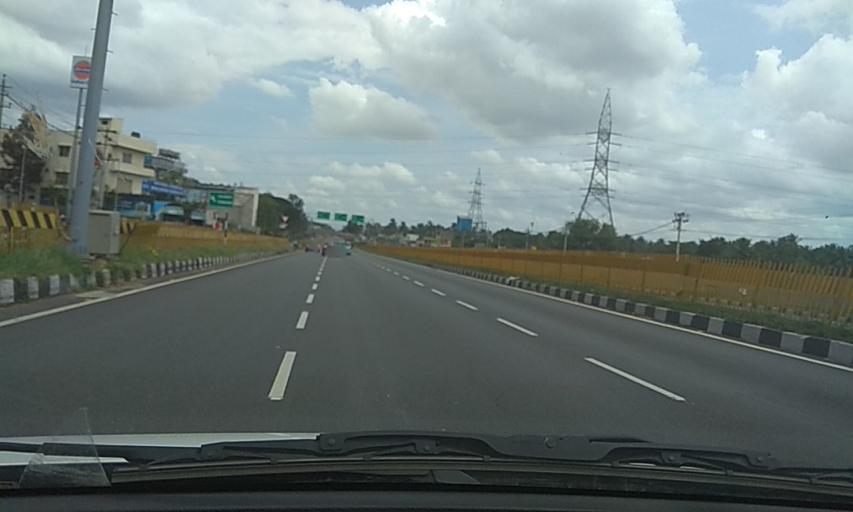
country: IN
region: Karnataka
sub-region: Tumkur
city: Tumkur
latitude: 13.3864
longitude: 77.0950
